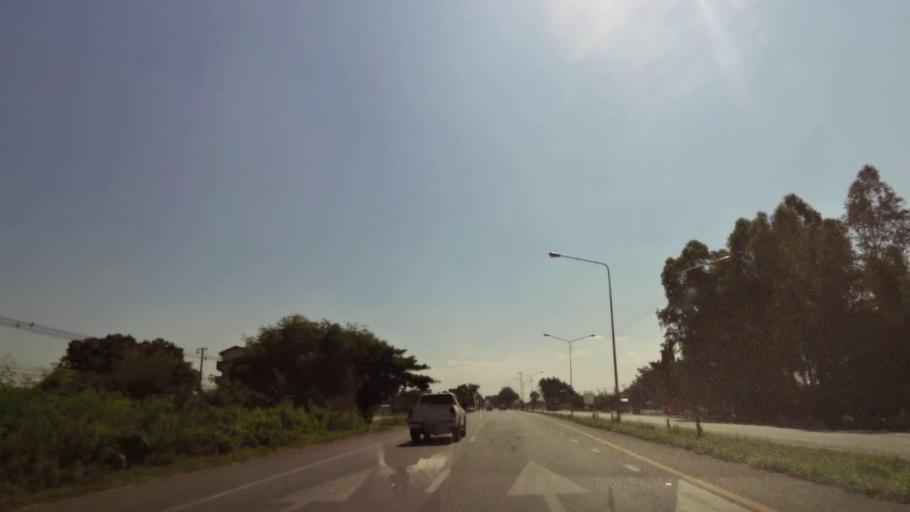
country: TH
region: Nakhon Sawan
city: Nakhon Sawan
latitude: 15.7760
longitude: 100.1213
